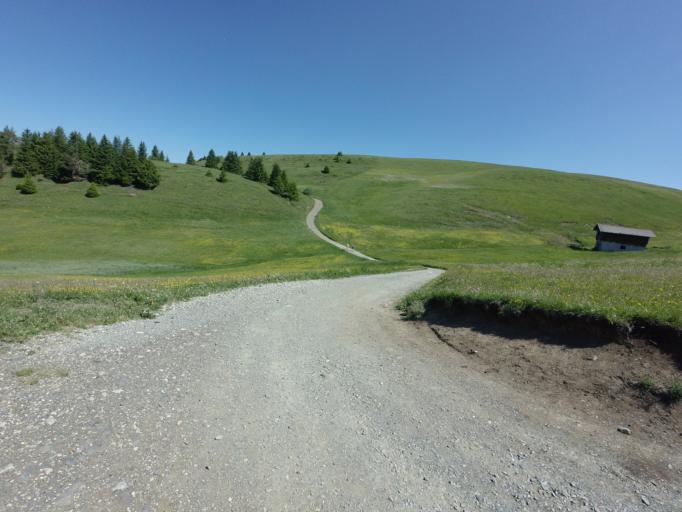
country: IT
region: Trentino-Alto Adige
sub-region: Bolzano
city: Siusi
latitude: 46.5497
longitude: 11.6040
